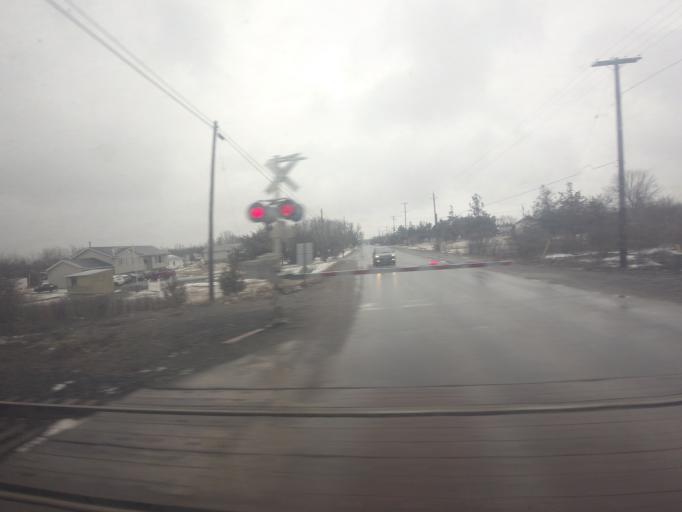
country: CA
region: Ontario
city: Belleville
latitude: 44.2042
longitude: -77.2352
